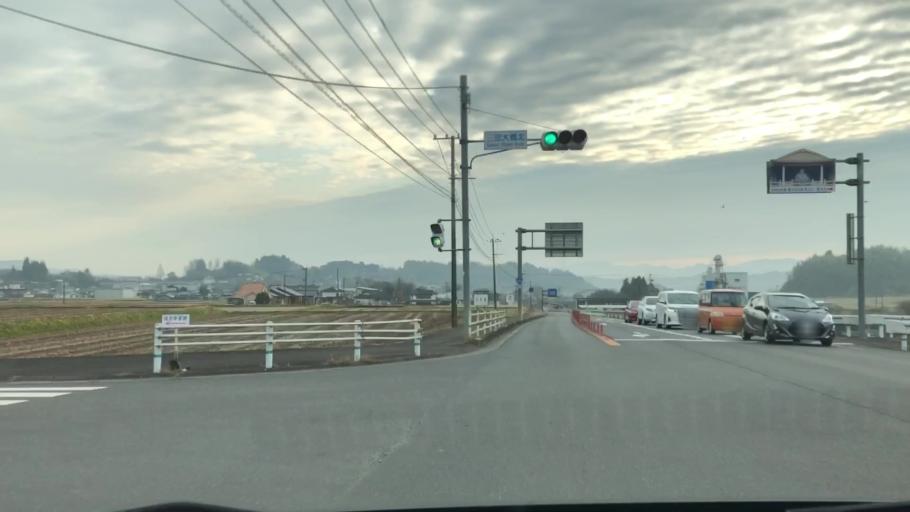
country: JP
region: Oita
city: Takedamachi
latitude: 32.9696
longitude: 131.4646
